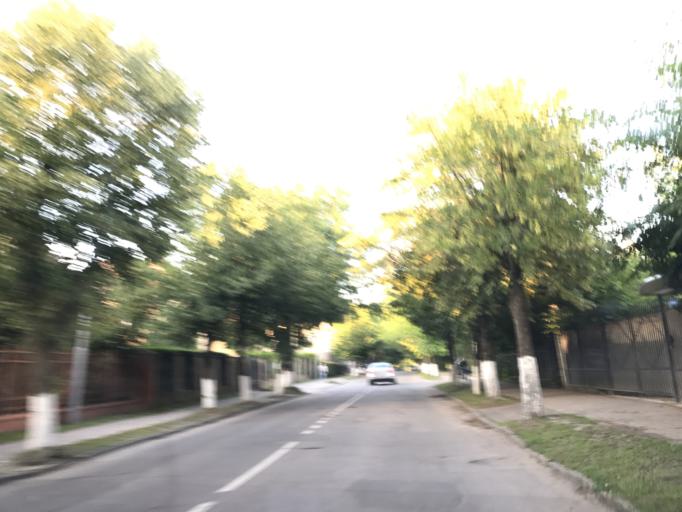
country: RU
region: Kaliningrad
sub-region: Zelenogradskiy Rayon
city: Zelenogradsk
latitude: 54.9568
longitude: 20.4666
